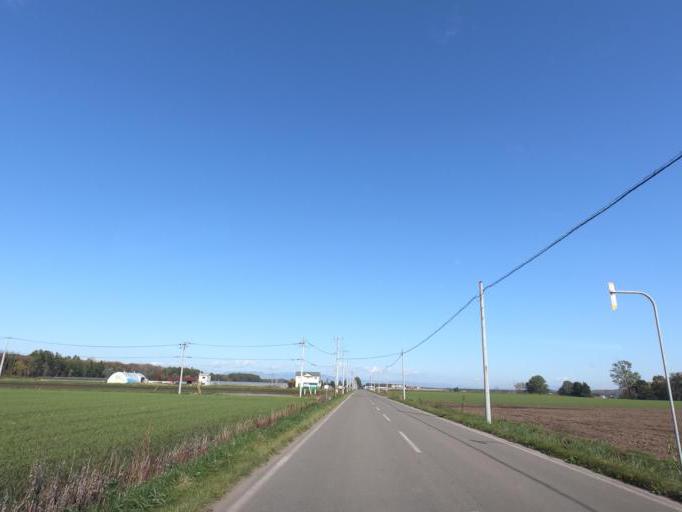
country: JP
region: Hokkaido
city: Obihiro
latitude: 42.9512
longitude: 143.2356
